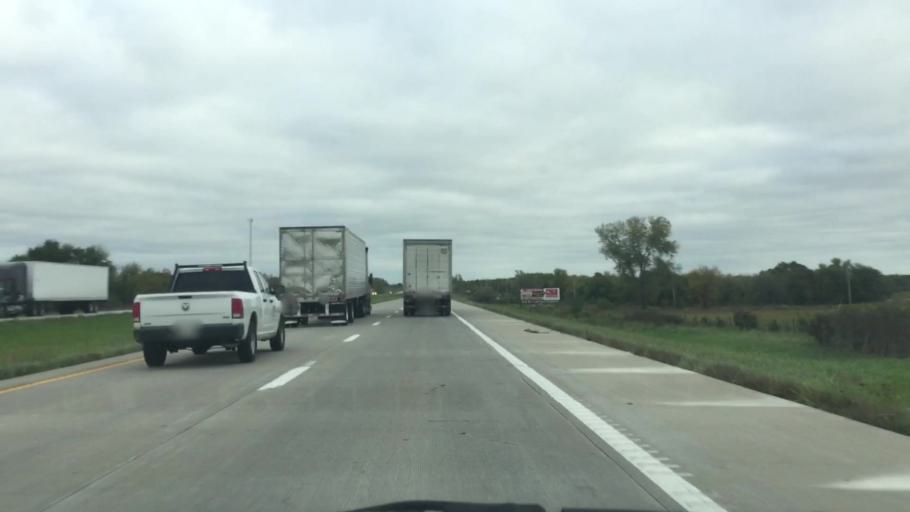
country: US
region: Missouri
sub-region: Clinton County
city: Lathrop
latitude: 39.5948
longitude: -94.2550
